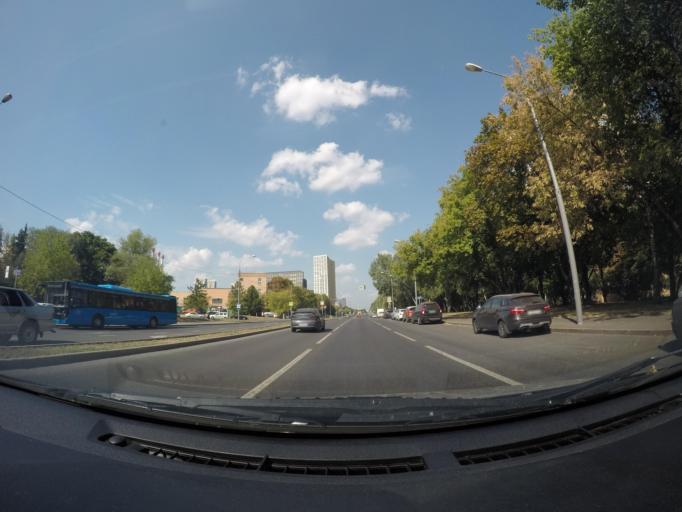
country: RU
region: Moskovskaya
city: Levoberezhnyy
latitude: 55.8630
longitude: 37.4860
